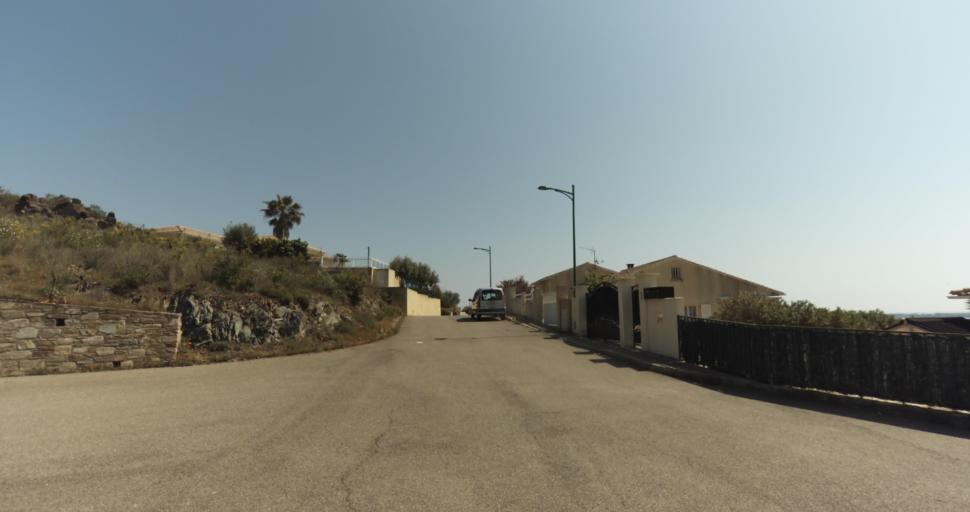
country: FR
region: Corsica
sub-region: Departement de la Haute-Corse
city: Biguglia
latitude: 42.6168
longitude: 9.4300
